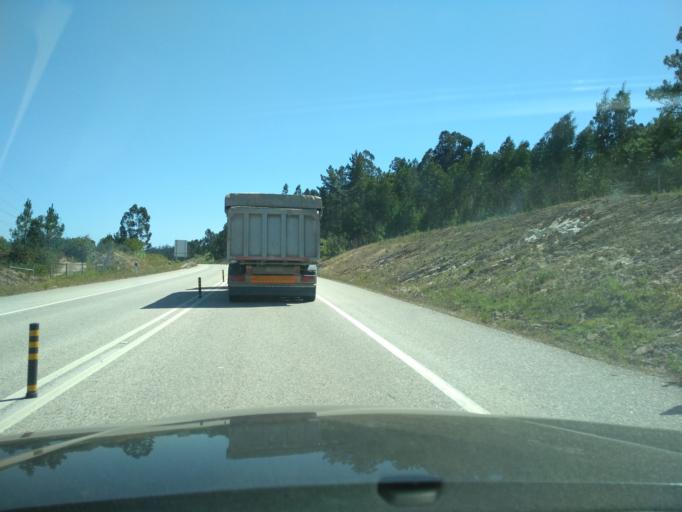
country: PT
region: Leiria
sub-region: Pombal
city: Lourical
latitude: 39.9558
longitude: -8.6907
